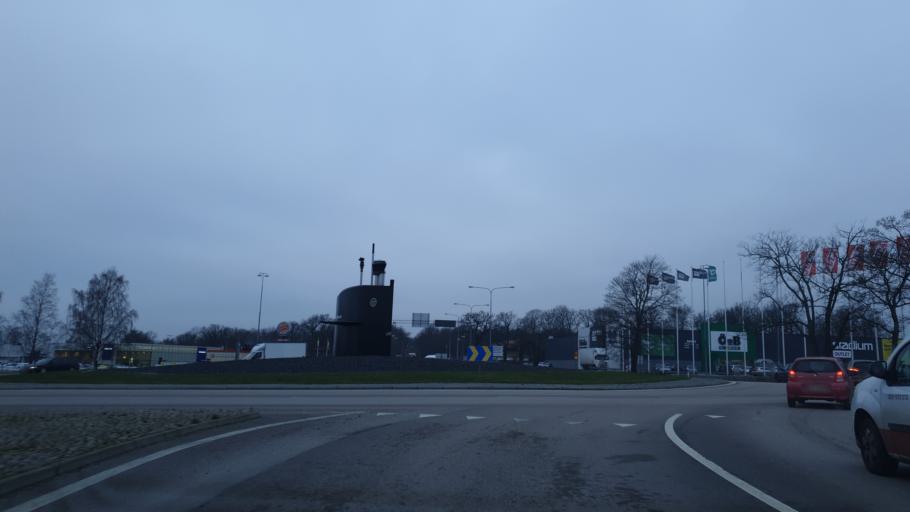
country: SE
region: Blekinge
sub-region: Karlskrona Kommun
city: Rodeby
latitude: 56.2033
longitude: 15.6403
